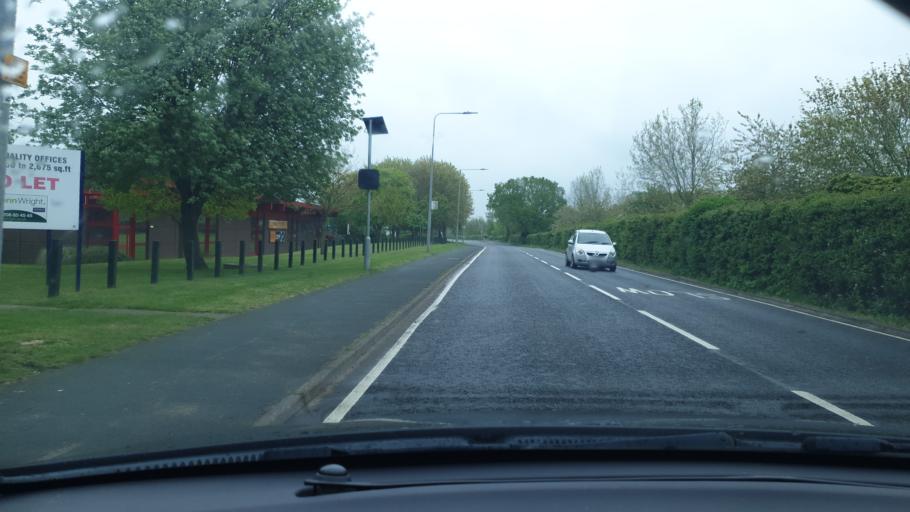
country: GB
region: England
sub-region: Essex
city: Colchester
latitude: 51.9162
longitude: 0.9245
